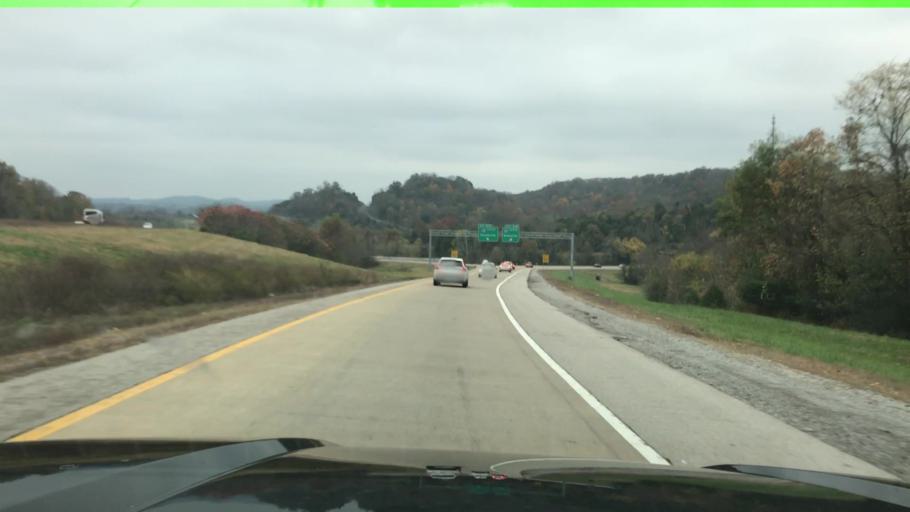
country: US
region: Tennessee
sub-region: Williamson County
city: Thompson's Station
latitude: 35.8227
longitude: -86.8288
